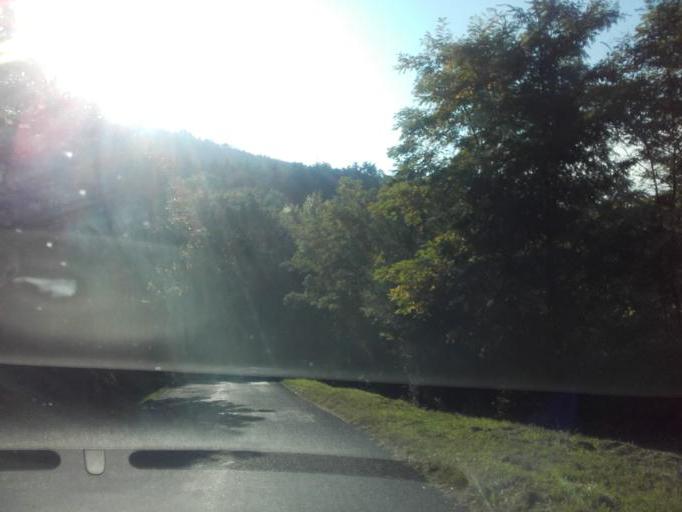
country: FR
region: Rhone-Alpes
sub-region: Departement du Rhone
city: Fleurie
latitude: 46.2291
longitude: 4.7088
